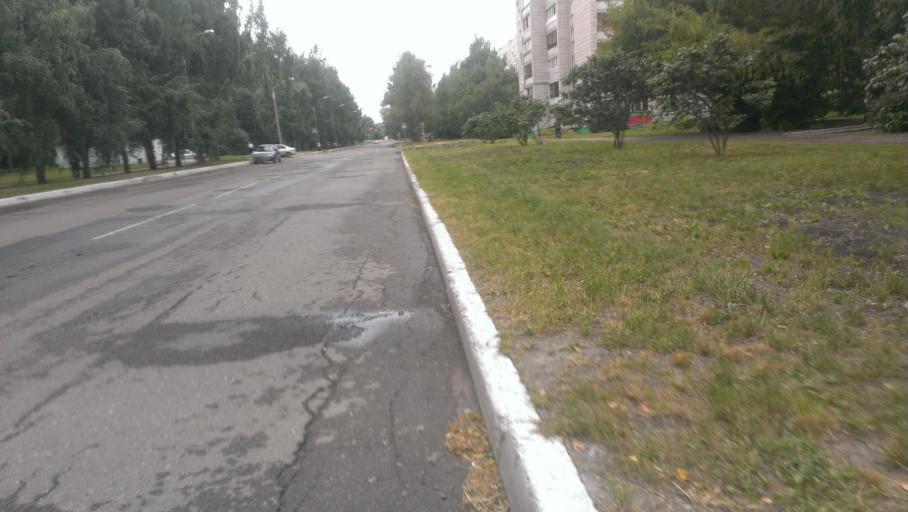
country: RU
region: Altai Krai
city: Novosilikatnyy
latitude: 53.3704
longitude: 83.6693
